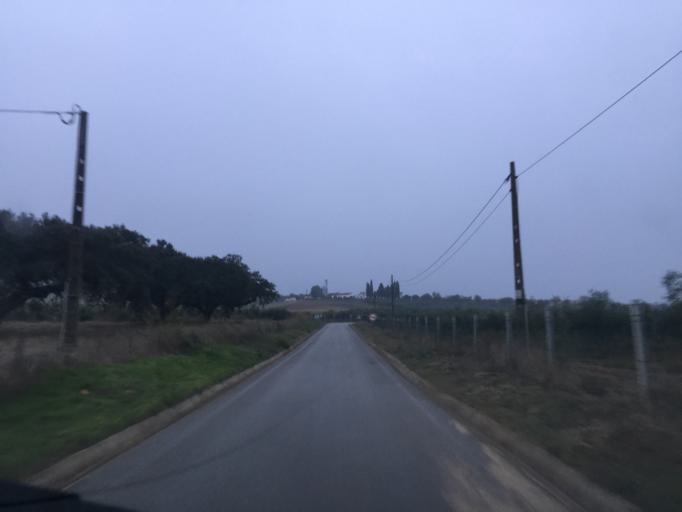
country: PT
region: Portalegre
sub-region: Avis
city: Avis
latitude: 39.0468
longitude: -7.9065
